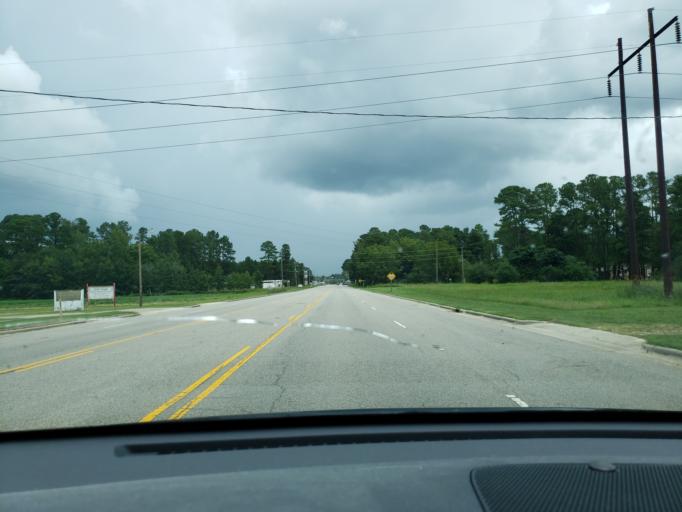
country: US
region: North Carolina
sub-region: Bladen County
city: Bladenboro
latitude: 34.4863
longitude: -78.6636
